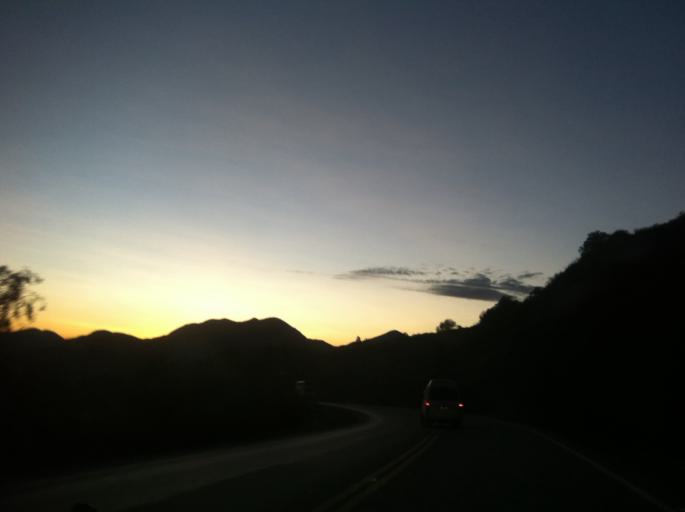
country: BO
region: Cochabamba
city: Irpa Irpa
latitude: -17.6628
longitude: -66.4188
